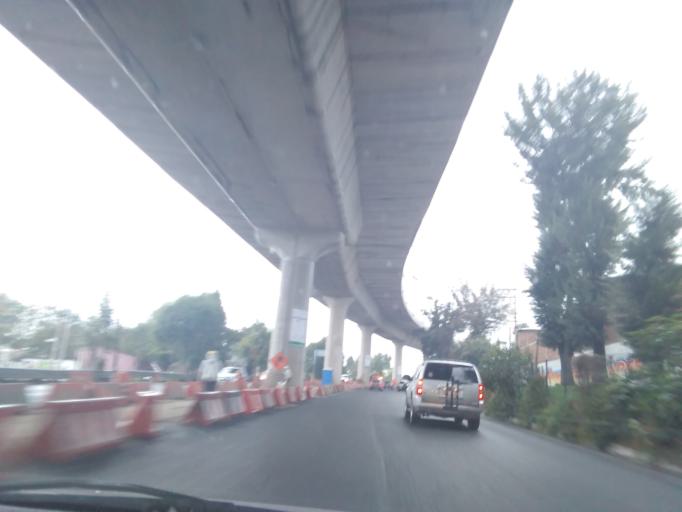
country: MX
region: Mexico City
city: Tlalpan
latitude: 19.2726
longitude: -99.1644
